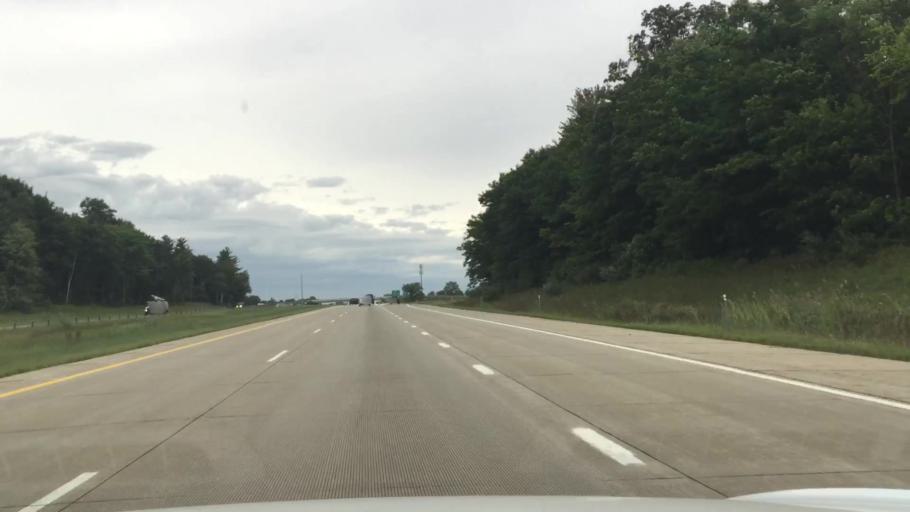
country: US
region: Michigan
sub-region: Saint Clair County
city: Marysville
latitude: 42.8674
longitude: -82.5507
